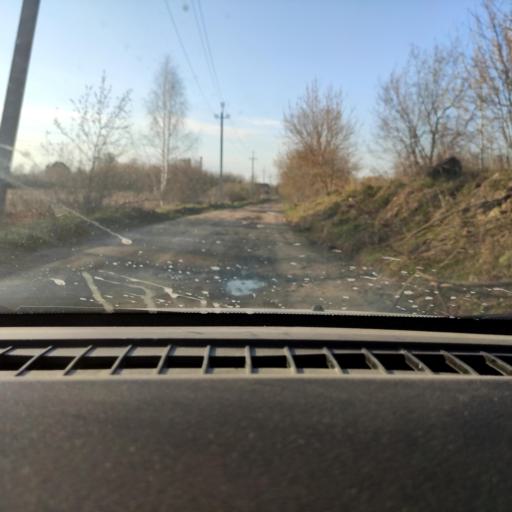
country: RU
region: Perm
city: Perm
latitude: 58.0246
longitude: 56.2108
